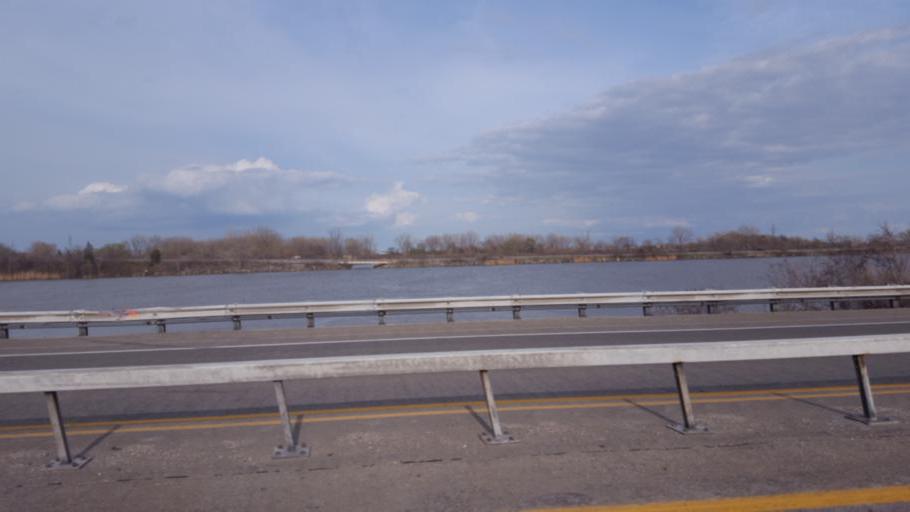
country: US
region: Ohio
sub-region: Ottawa County
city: Port Clinton
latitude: 41.4958
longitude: -82.8364
